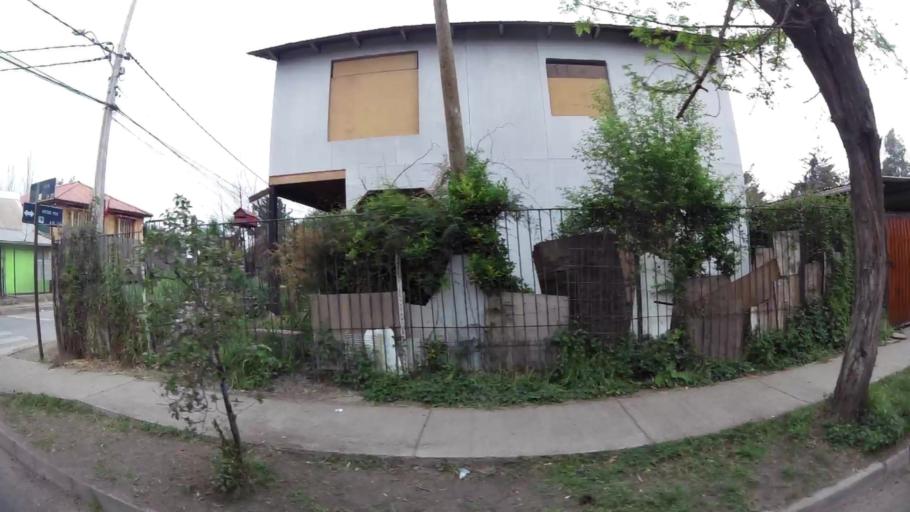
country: CL
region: Santiago Metropolitan
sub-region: Provincia de Chacabuco
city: Lampa
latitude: -33.2362
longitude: -70.8065
